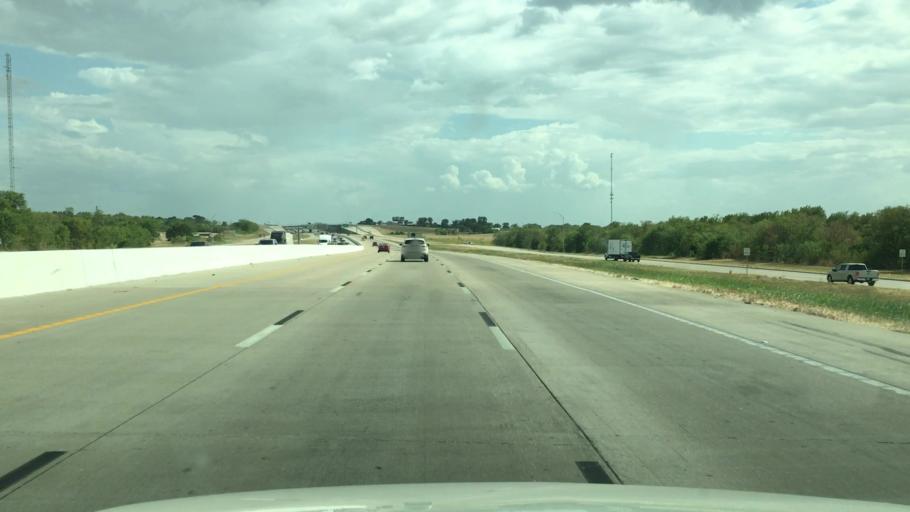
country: US
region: Texas
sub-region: McLennan County
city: West
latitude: 31.7969
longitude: -97.1023
